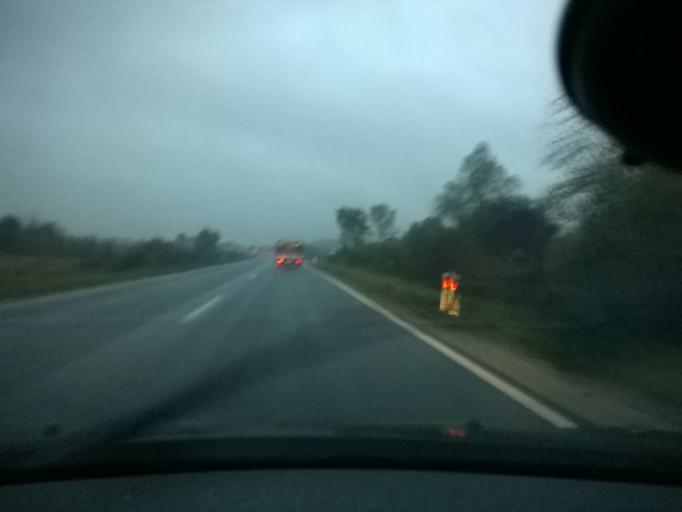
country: HR
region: Zagrebacka
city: Jakovlje
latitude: 45.9396
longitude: 15.8217
